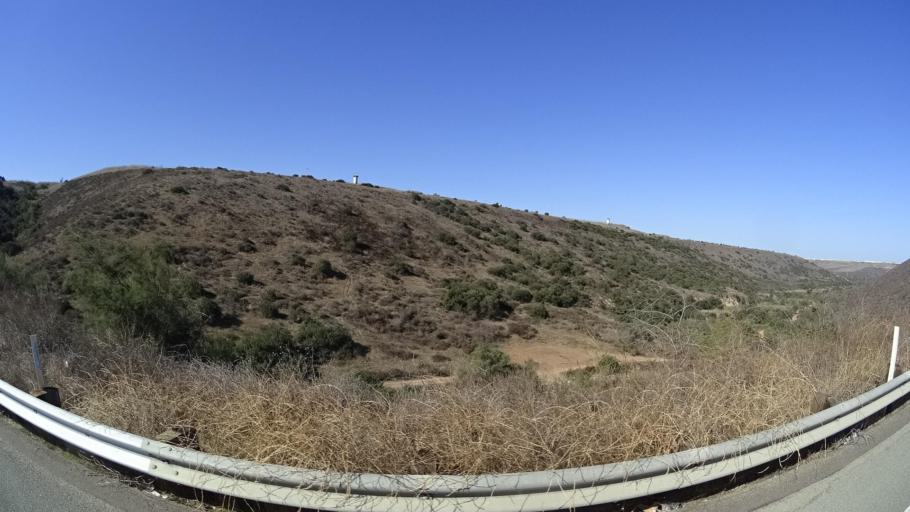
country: MX
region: Baja California
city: Tijuana
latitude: 32.5870
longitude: -116.9266
